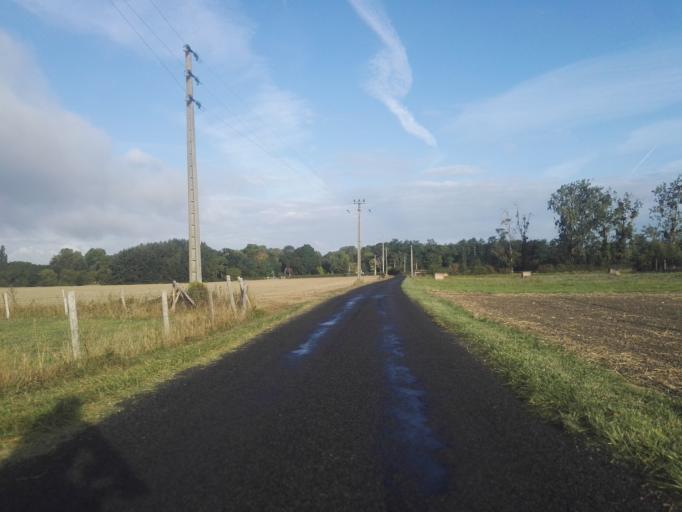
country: FR
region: Haute-Normandie
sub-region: Departement de l'Eure
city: Menilles
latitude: 49.0349
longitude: 1.3496
